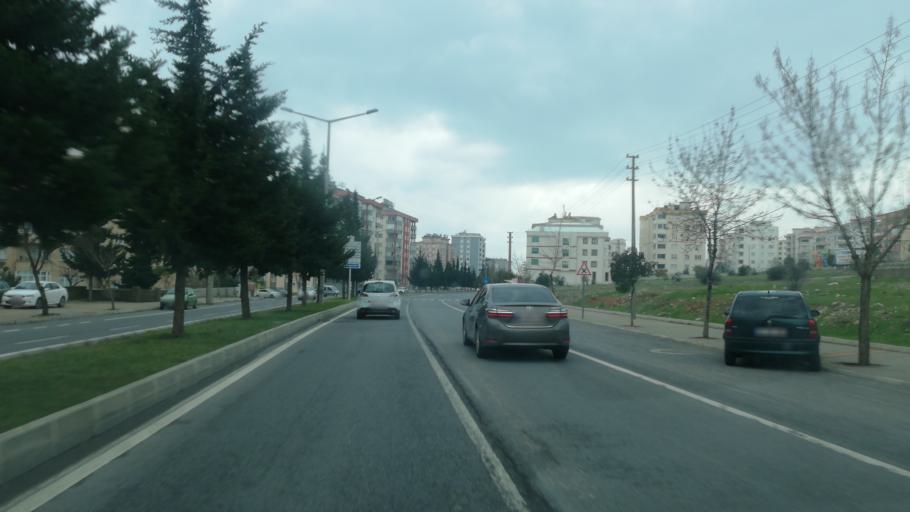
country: TR
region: Kahramanmaras
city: Kahramanmaras
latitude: 37.5911
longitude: 36.8947
